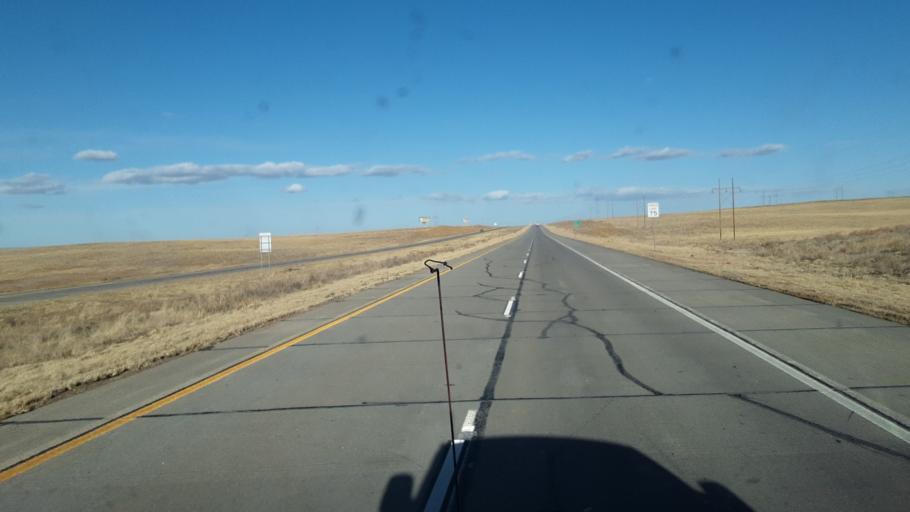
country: US
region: Colorado
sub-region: Logan County
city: Sterling
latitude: 40.7140
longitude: -103.0463
